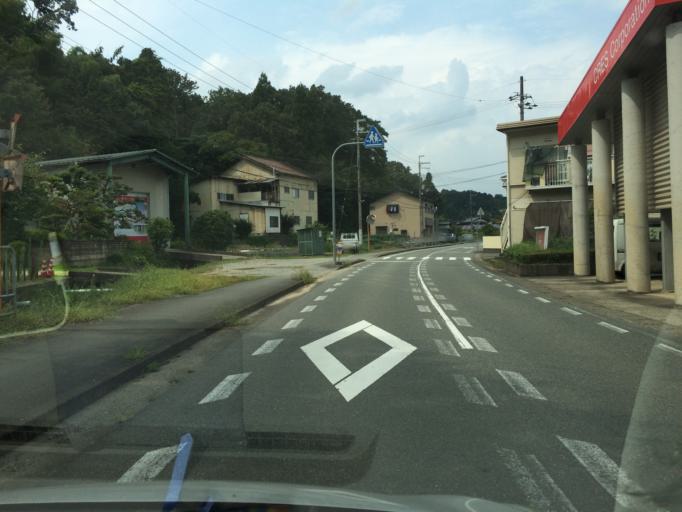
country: JP
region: Hyogo
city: Toyooka
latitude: 35.5232
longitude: 134.8184
